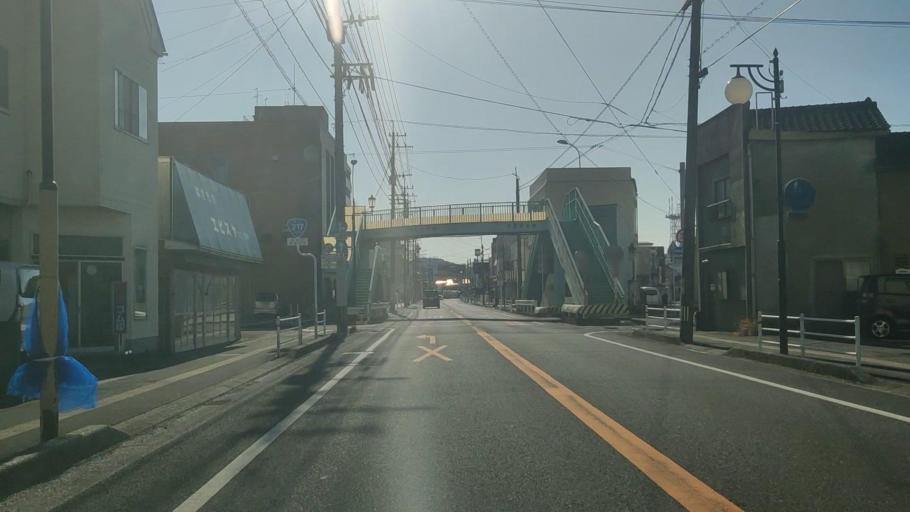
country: JP
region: Oita
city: Saiki
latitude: 32.9639
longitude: 131.9005
